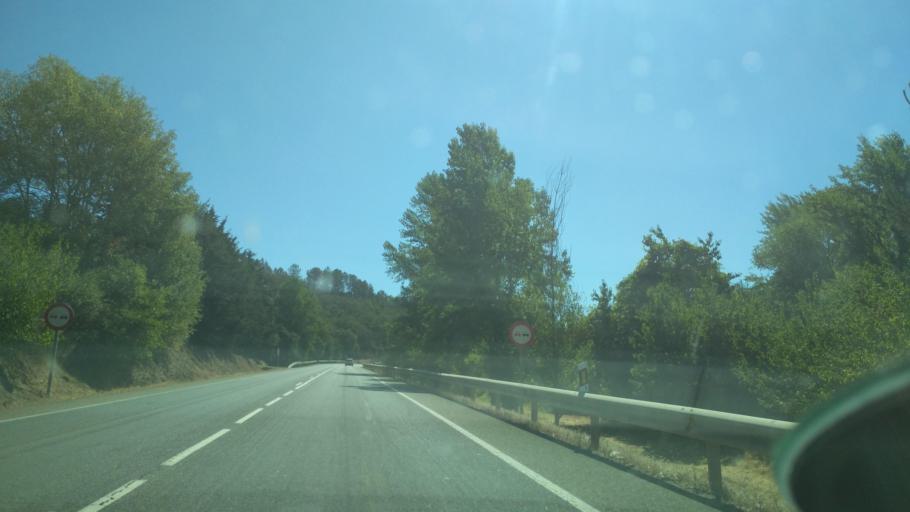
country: ES
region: Andalusia
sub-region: Provincia de Huelva
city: Fuenteheridos
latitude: 37.9167
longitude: -6.6743
